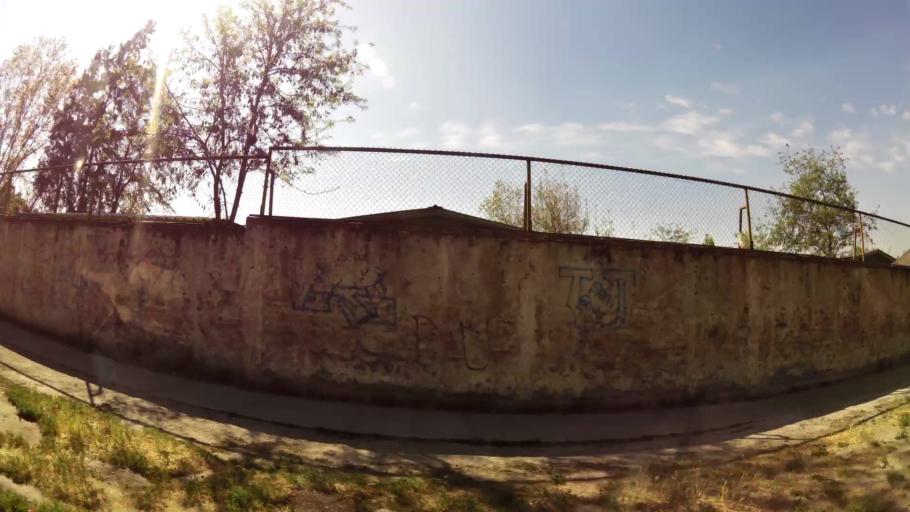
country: CL
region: Santiago Metropolitan
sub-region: Provincia de Santiago
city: La Pintana
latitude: -33.5390
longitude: -70.6149
